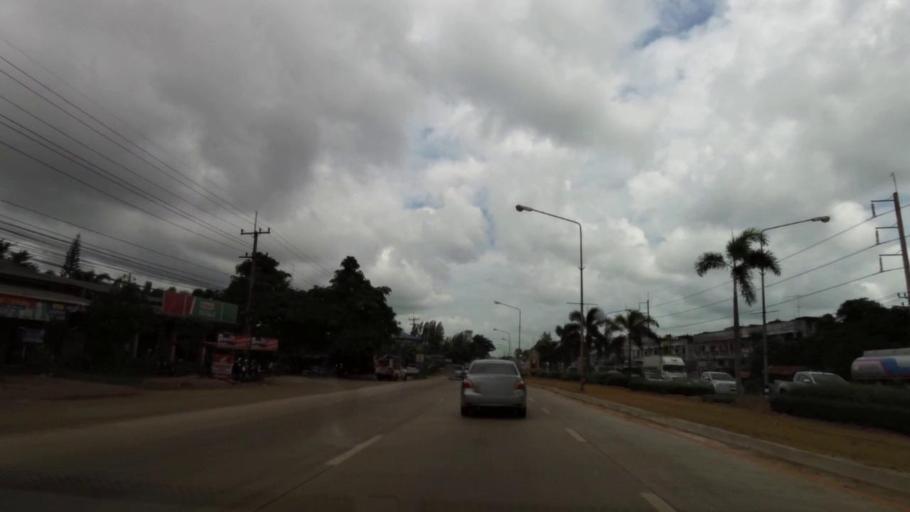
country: TH
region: Chanthaburi
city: Na Yai Am
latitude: 12.7820
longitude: 101.8072
